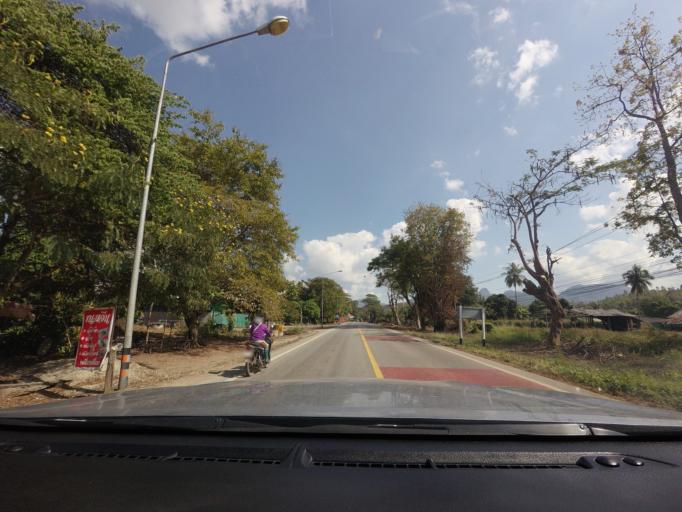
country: TH
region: Chiang Mai
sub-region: Amphoe Chiang Dao
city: Chiang Dao
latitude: 19.4817
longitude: 99.0184
